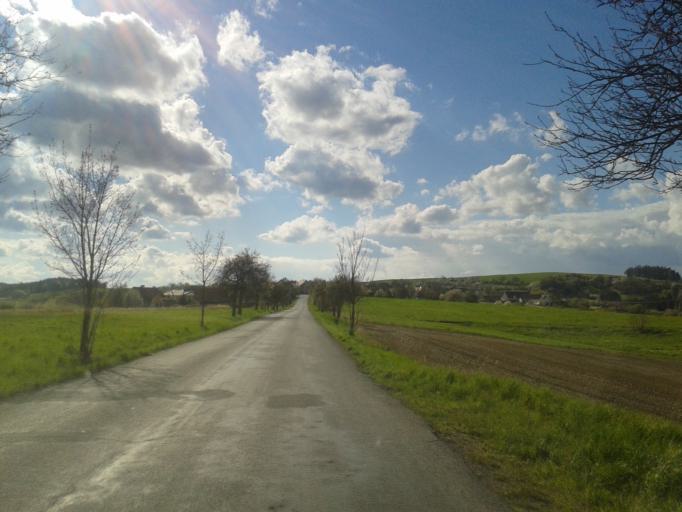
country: CZ
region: Central Bohemia
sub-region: Okres Beroun
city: Lodenice
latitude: 50.0104
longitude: 14.1245
